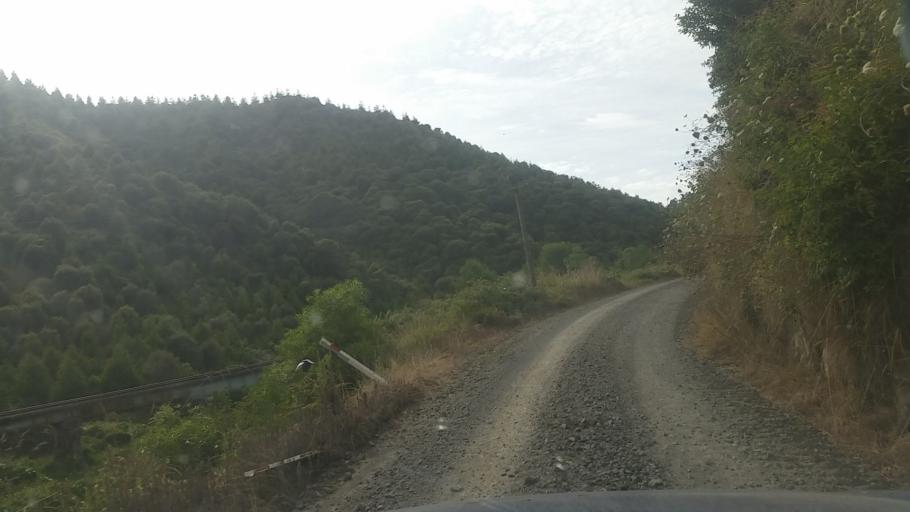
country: NZ
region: Taranaki
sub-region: New Plymouth District
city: Waitara
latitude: -39.1411
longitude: 174.7188
